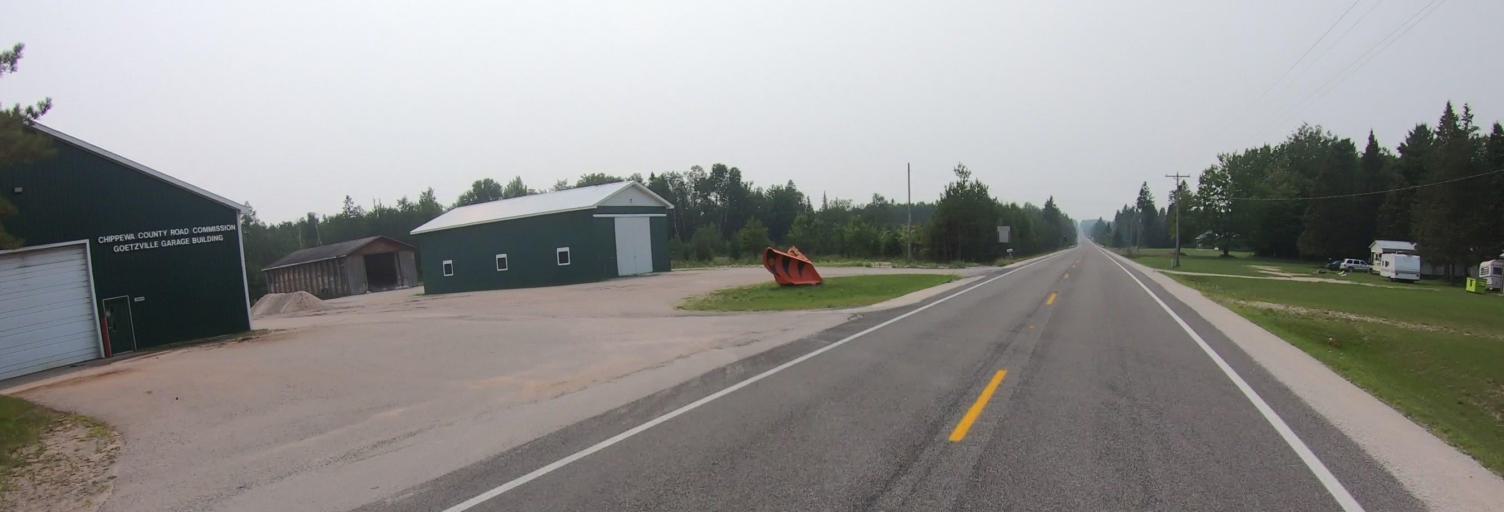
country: US
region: Michigan
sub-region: Chippewa County
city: Sault Ste. Marie
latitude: 46.0724
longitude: -84.1081
